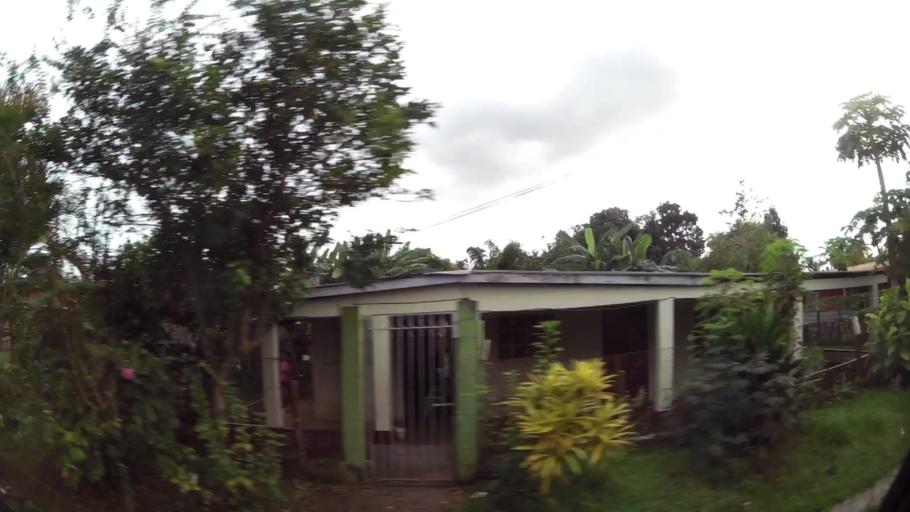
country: PA
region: Panama
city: Tocumen
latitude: 9.1019
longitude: -79.3787
